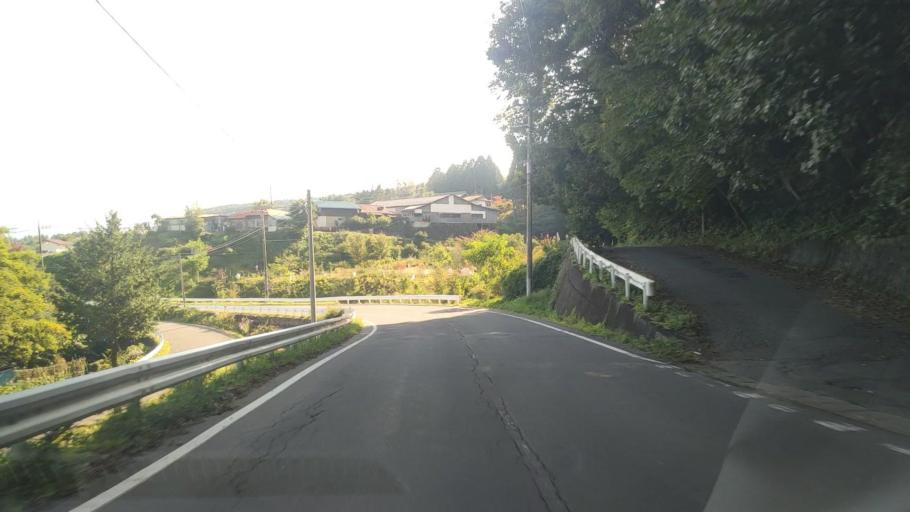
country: JP
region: Nagano
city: Suzaka
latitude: 36.5659
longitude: 138.5542
